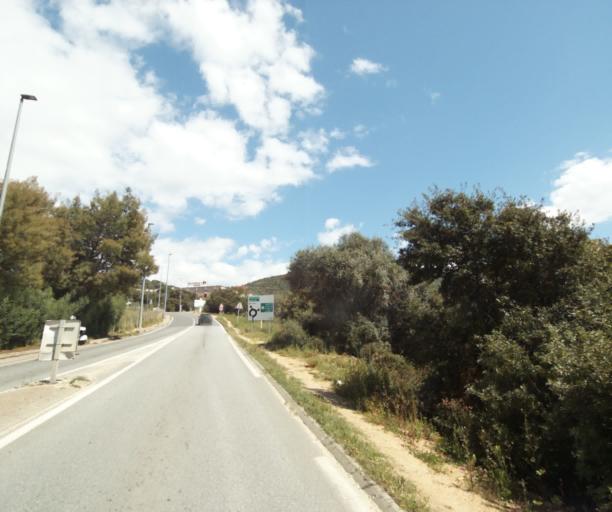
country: FR
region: Corsica
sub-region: Departement de la Corse-du-Sud
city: Propriano
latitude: 41.6663
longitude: 8.9204
